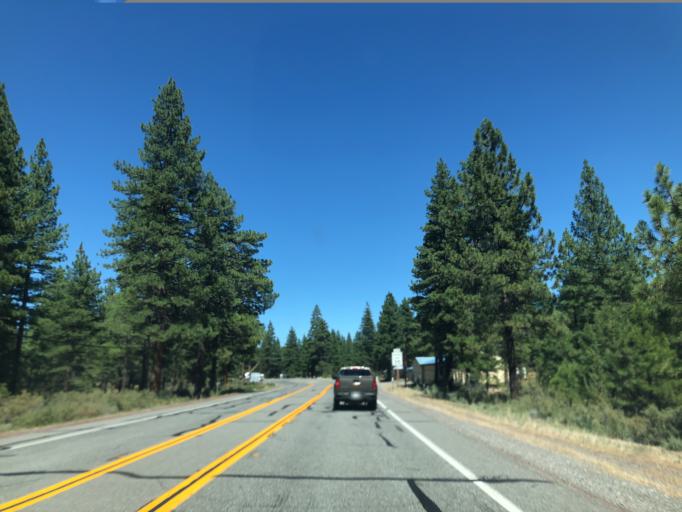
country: US
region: California
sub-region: Lassen County
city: Susanville
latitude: 40.4192
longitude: -120.7063
